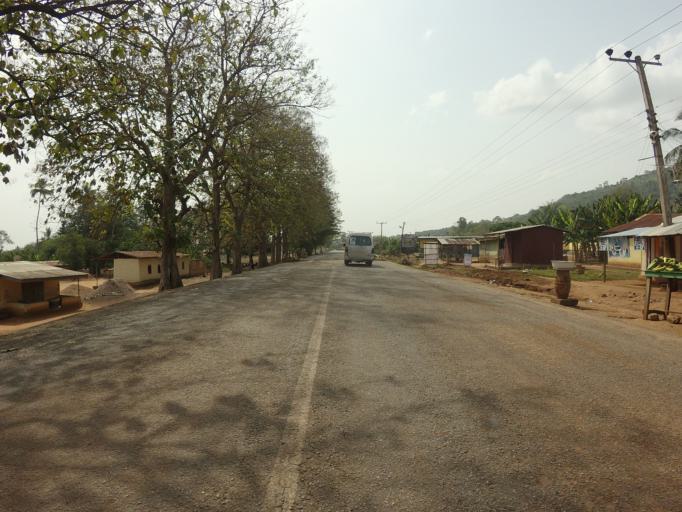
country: GH
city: Akropong
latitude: 6.2828
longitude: 0.1318
